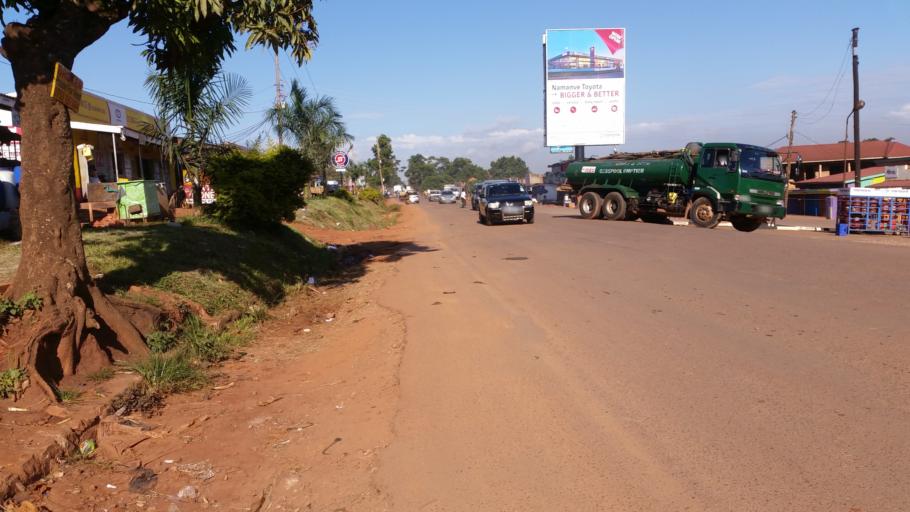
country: UG
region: Central Region
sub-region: Wakiso District
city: Kireka
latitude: 0.3437
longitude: 32.6466
